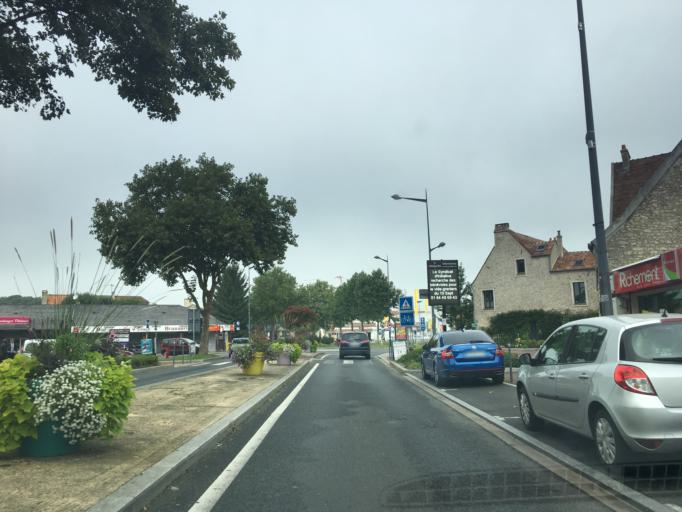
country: FR
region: Ile-de-France
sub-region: Departement de Seine-et-Marne
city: Brie-Comte-Robert
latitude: 48.6964
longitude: 2.6079
